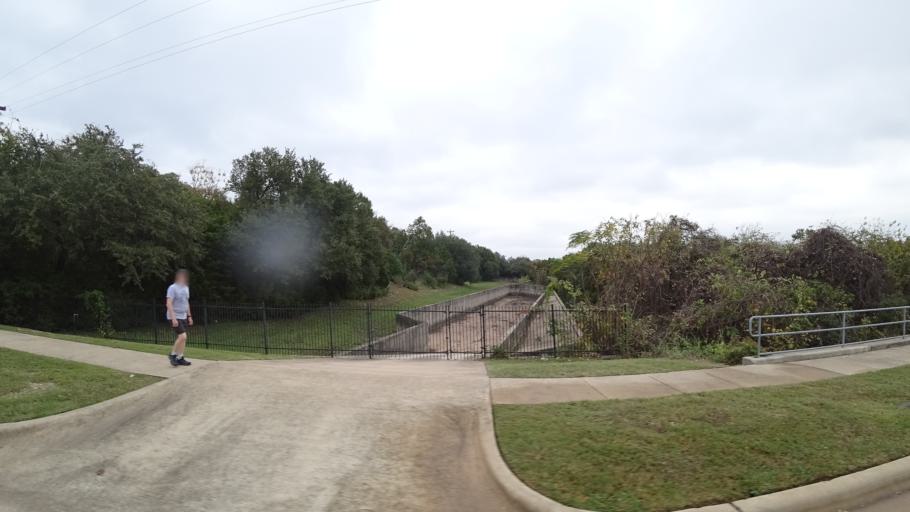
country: US
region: Texas
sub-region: Williamson County
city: Anderson Mill
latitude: 30.4334
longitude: -97.8304
